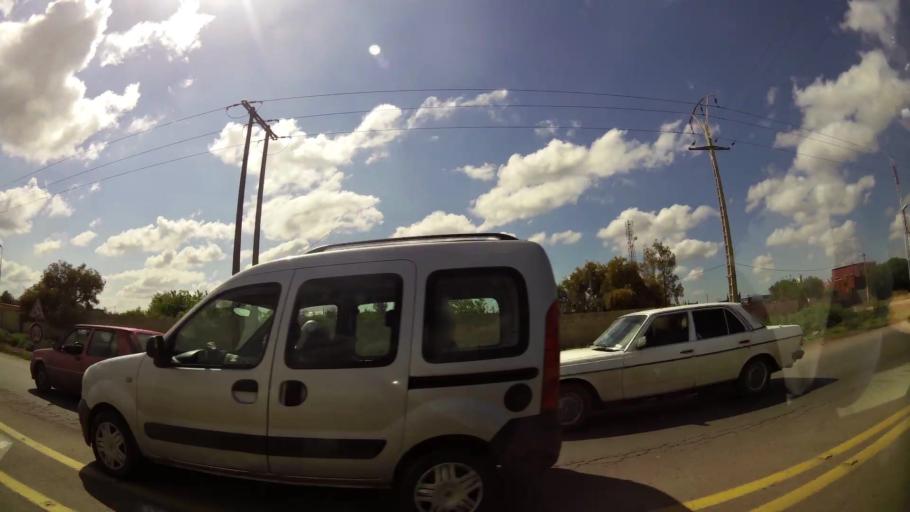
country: MA
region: Grand Casablanca
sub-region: Mediouna
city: Mediouna
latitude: 33.4108
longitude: -7.5329
